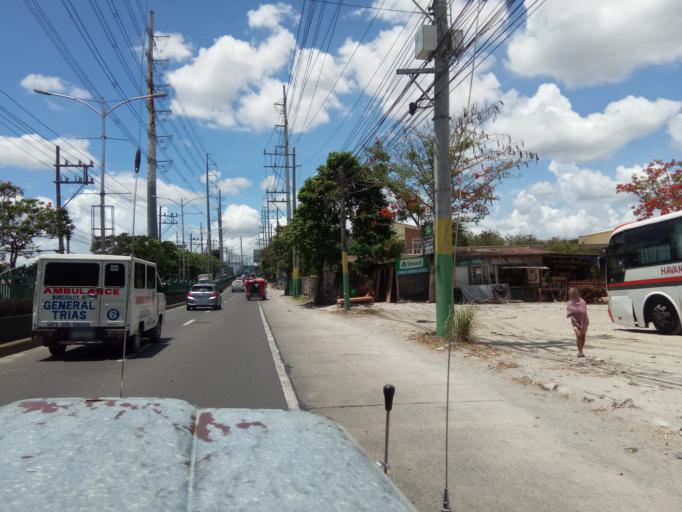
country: PH
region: Calabarzon
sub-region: Province of Cavite
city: Dasmarinas
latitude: 14.3216
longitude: 120.9415
